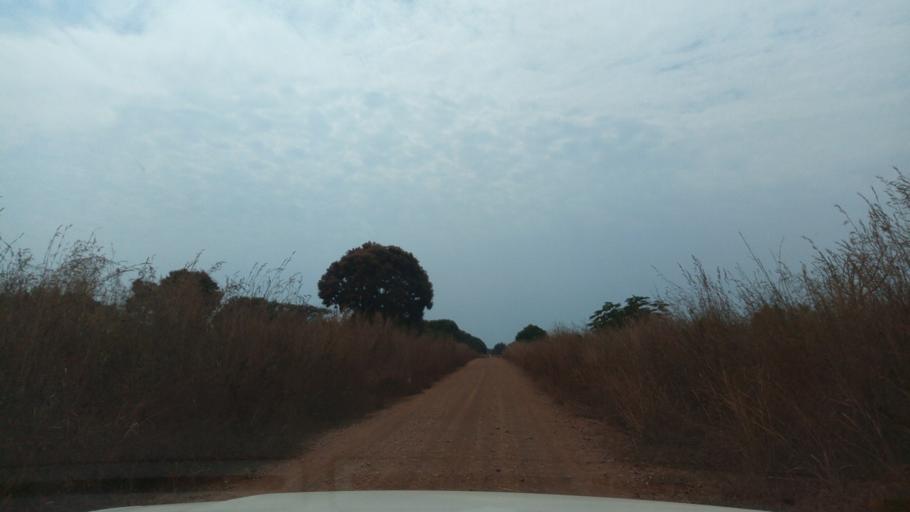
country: ZM
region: Northern
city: Kaputa
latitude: -8.3745
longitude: 28.9623
